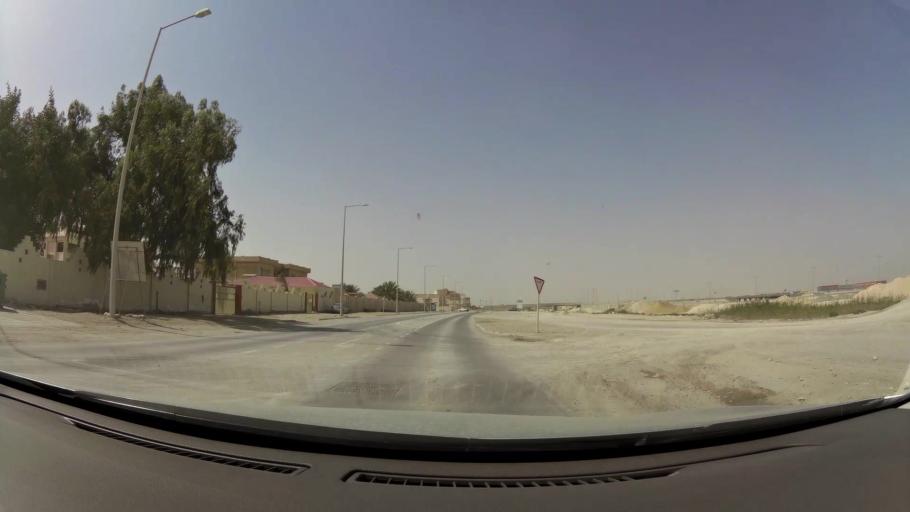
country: QA
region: Baladiyat Umm Salal
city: Umm Salal Muhammad
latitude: 25.3736
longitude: 51.4397
